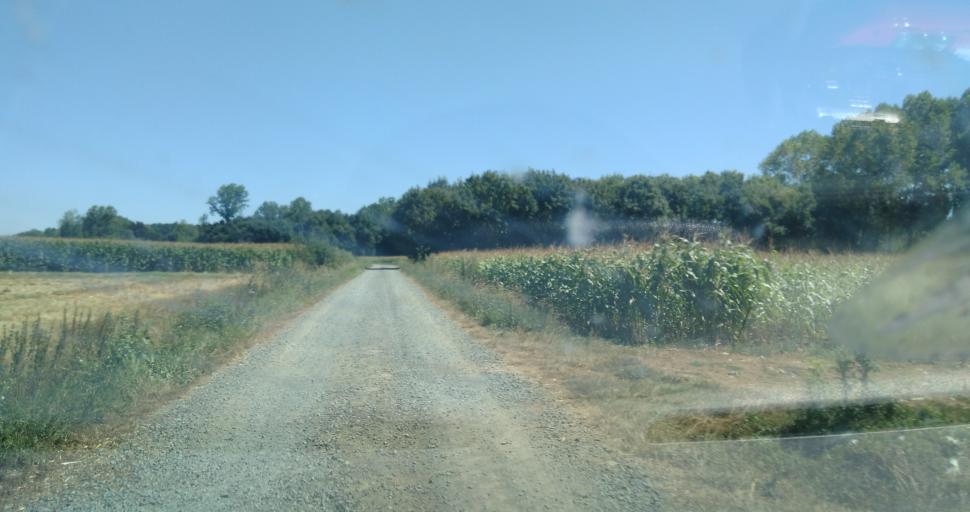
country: FR
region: Pays de la Loire
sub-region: Departement de la Vendee
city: Sainte-Hermine
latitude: 46.5592
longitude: -1.0313
